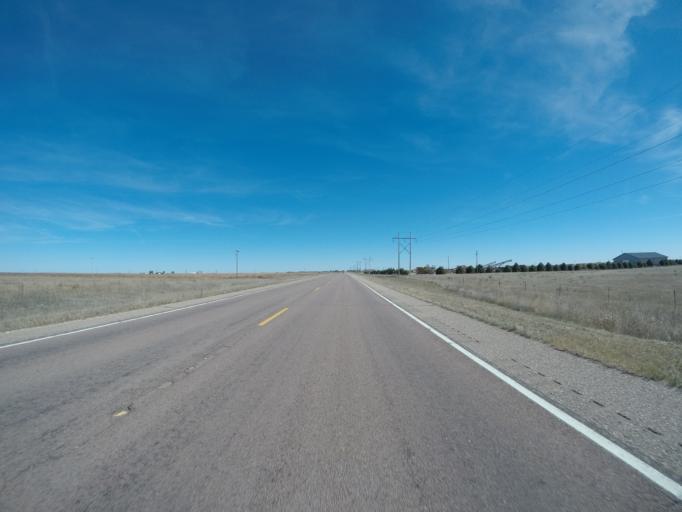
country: US
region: Colorado
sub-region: Yuma County
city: Yuma
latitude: 39.6558
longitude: -102.7178
